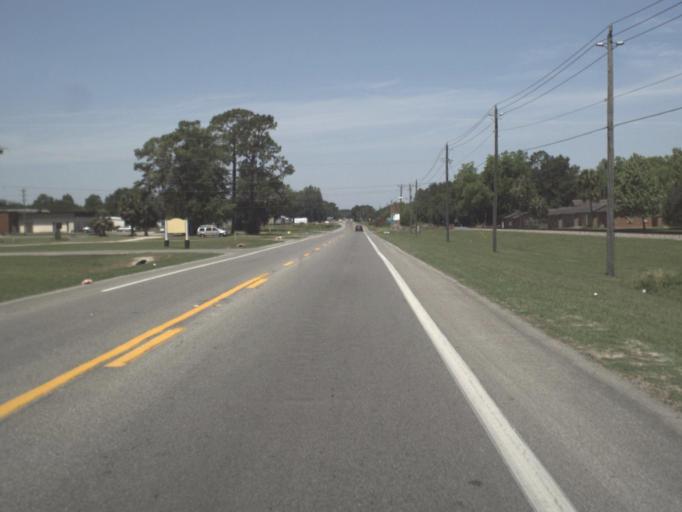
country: US
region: Florida
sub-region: Suwannee County
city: Live Oak
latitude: 30.3058
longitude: -83.0056
